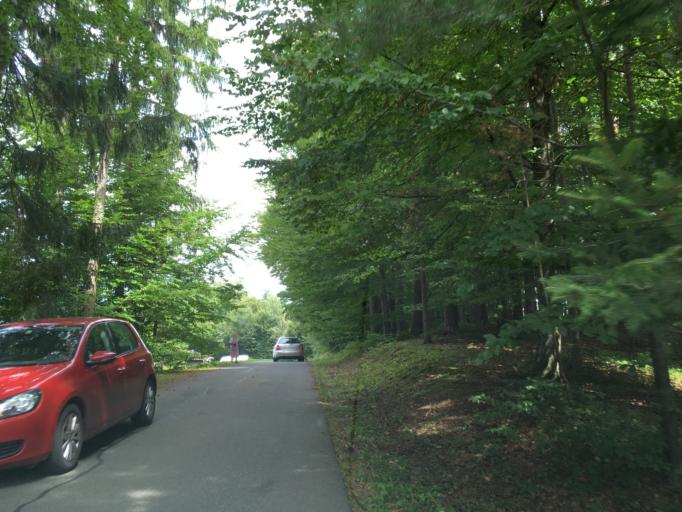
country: AT
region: Styria
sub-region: Politischer Bezirk Deutschlandsberg
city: Wettmannstatten
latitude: 46.7985
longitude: 15.3998
